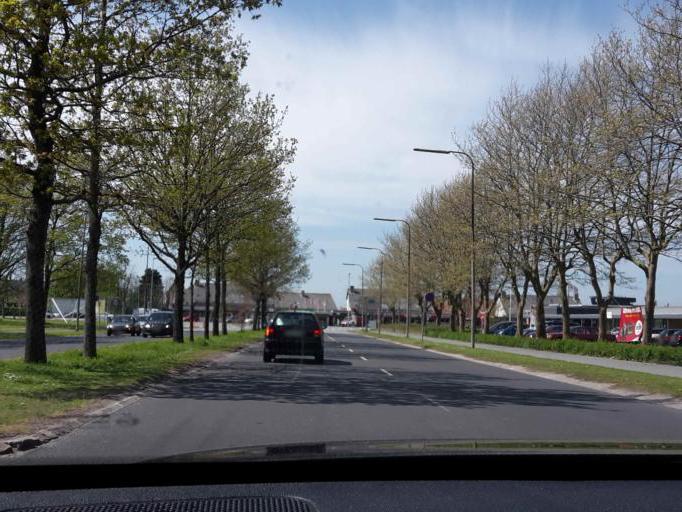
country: DK
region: South Denmark
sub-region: Odense Kommune
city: Odense
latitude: 55.3747
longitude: 10.3985
